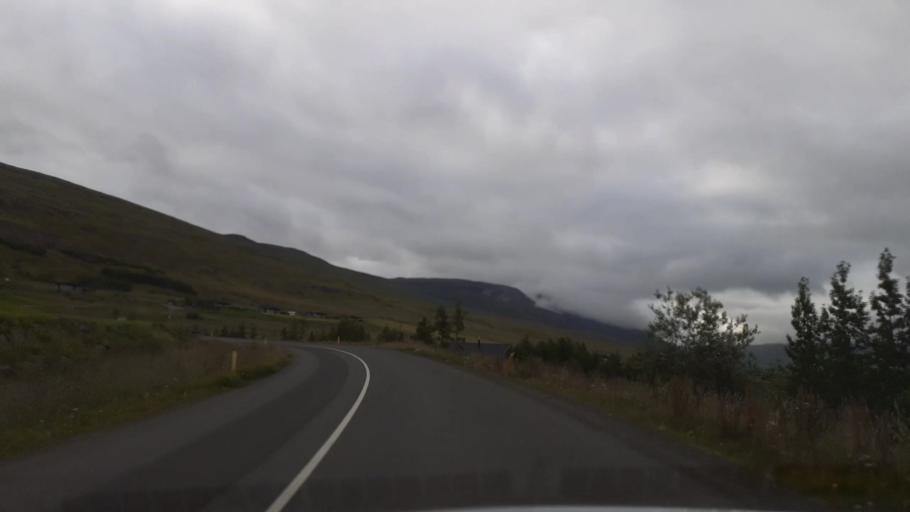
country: IS
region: Northeast
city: Akureyri
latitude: 65.6800
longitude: -18.0408
